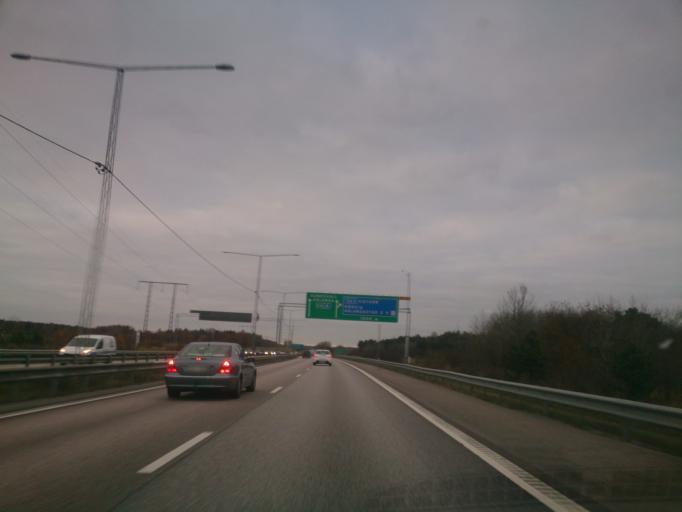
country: SE
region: Stockholm
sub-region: Sigtuna Kommun
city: Rosersberg
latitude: 59.5850
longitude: 17.9002
